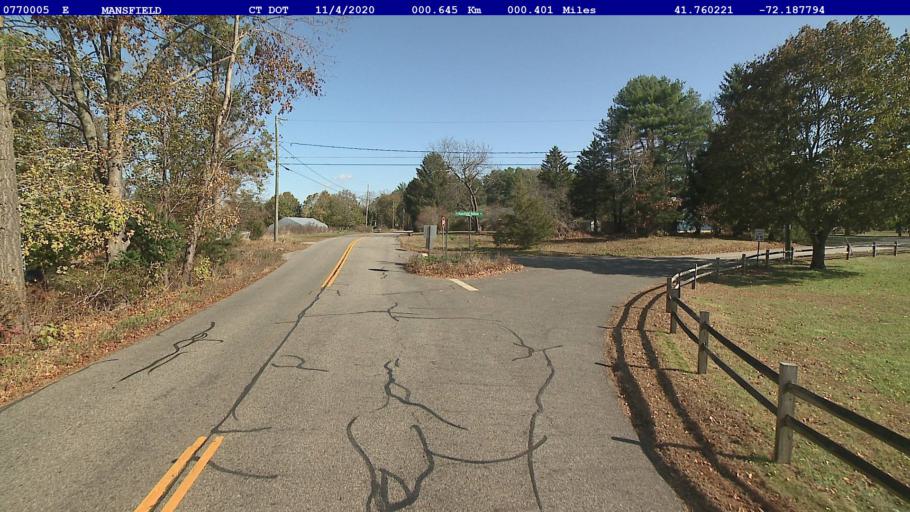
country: US
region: Connecticut
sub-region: Tolland County
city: Mansfield City
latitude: 41.7602
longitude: -72.1878
